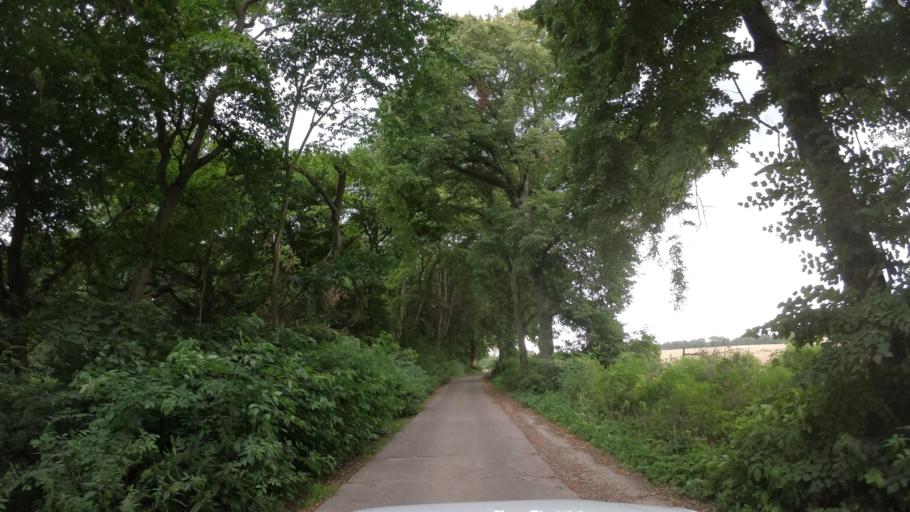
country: PL
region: West Pomeranian Voivodeship
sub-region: Powiat stargardzki
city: Dolice
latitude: 53.1900
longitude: 15.2953
